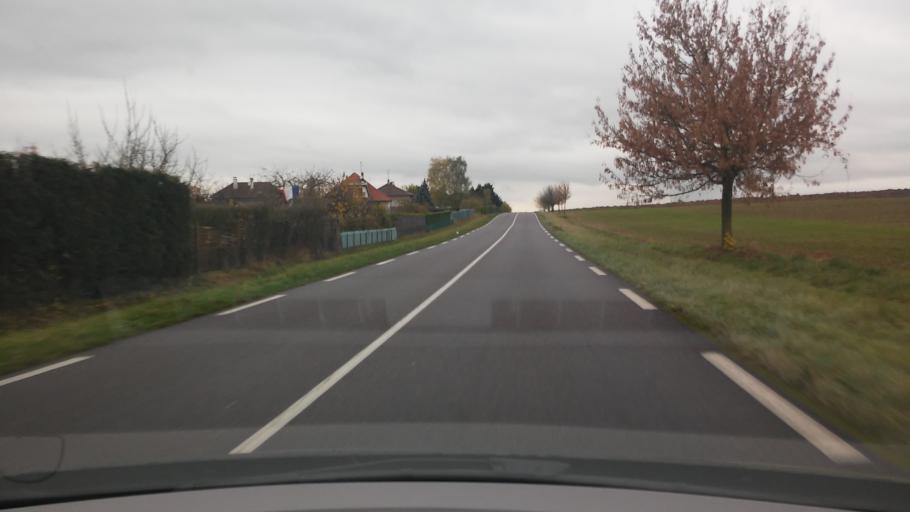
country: FR
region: Lorraine
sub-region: Departement de la Moselle
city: Bousse
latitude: 49.2698
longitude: 6.2021
